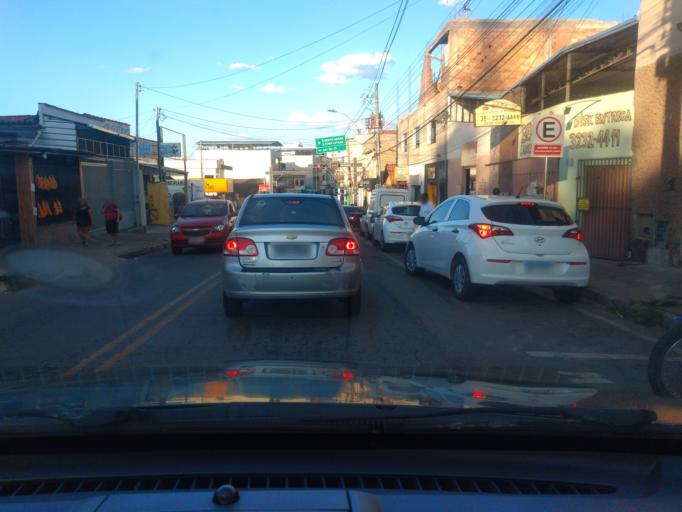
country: BR
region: Minas Gerais
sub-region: Tres Coracoes
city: Tres Coracoes
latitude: -21.6936
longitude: -45.2491
